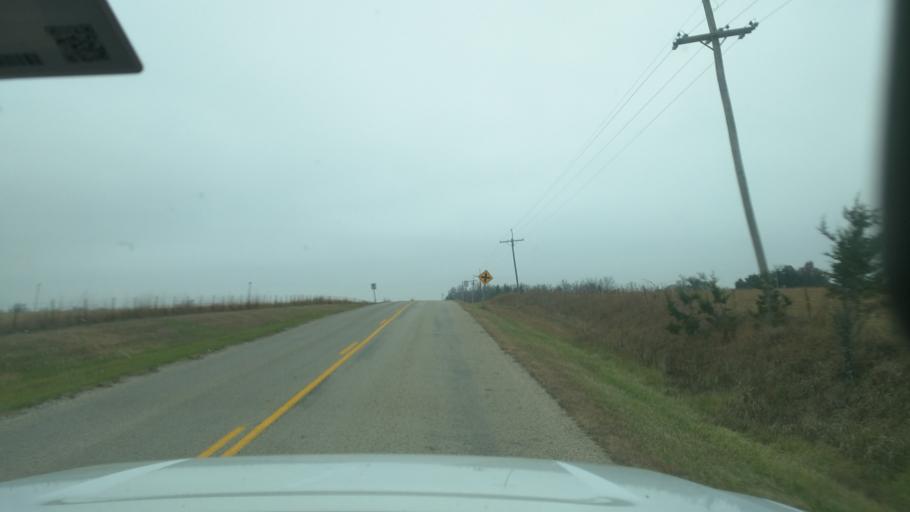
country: US
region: Kansas
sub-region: Morris County
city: Council Grove
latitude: 38.6247
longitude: -96.2614
